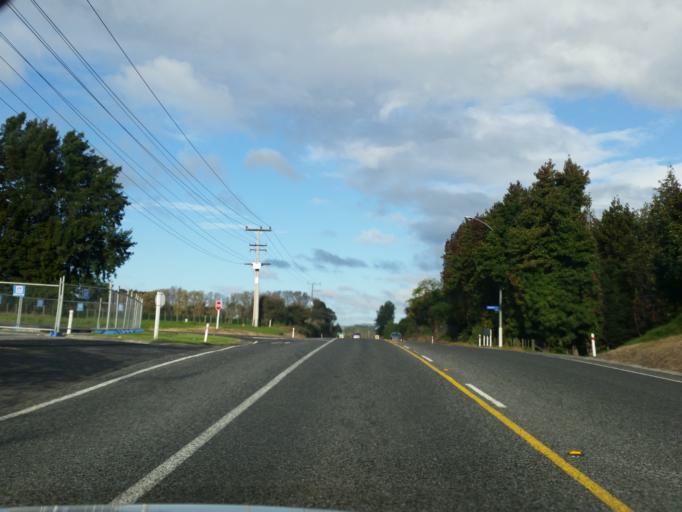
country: NZ
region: Bay of Plenty
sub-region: Western Bay of Plenty District
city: Katikati
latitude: -37.6623
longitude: 176.0103
